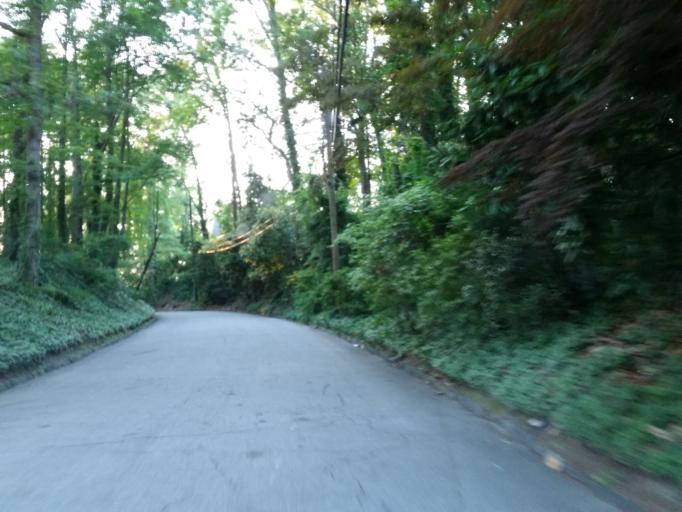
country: US
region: Georgia
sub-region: Cobb County
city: Vinings
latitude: 33.8662
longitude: -84.4356
